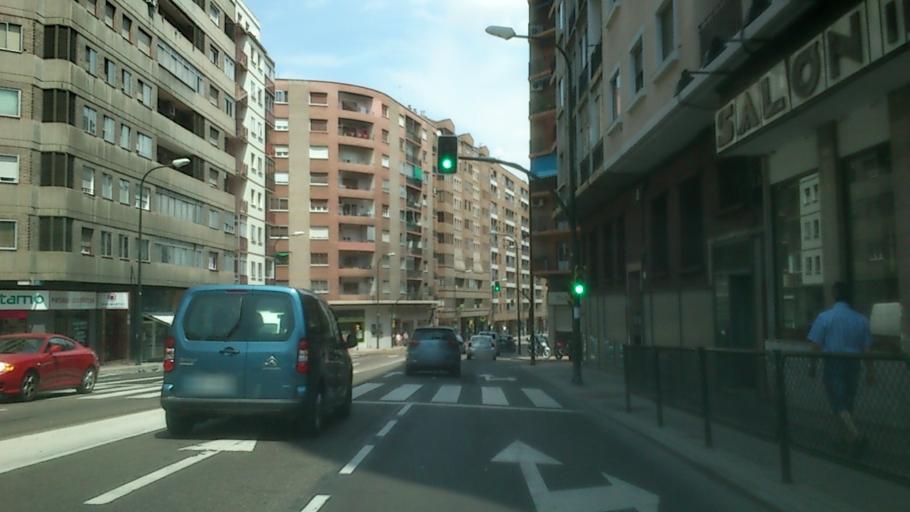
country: ES
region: Aragon
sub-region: Provincia de Zaragoza
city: Almozara
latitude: 41.6563
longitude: -0.8936
